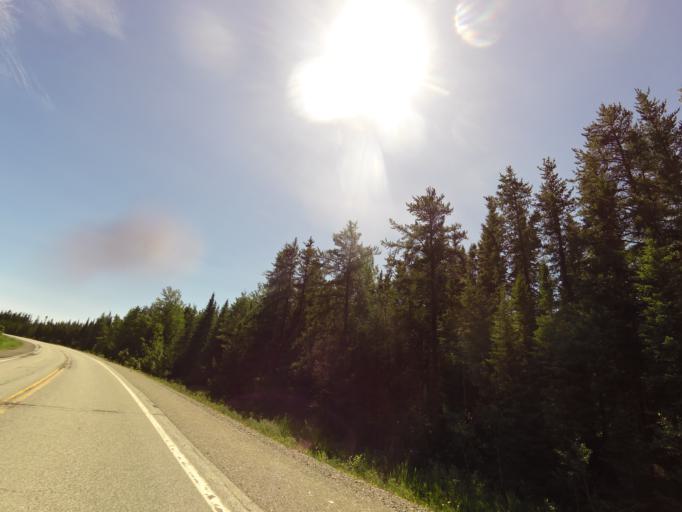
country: CA
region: Quebec
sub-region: Nord-du-Quebec
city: Lebel-sur-Quevillon
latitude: 48.8184
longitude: -77.1266
